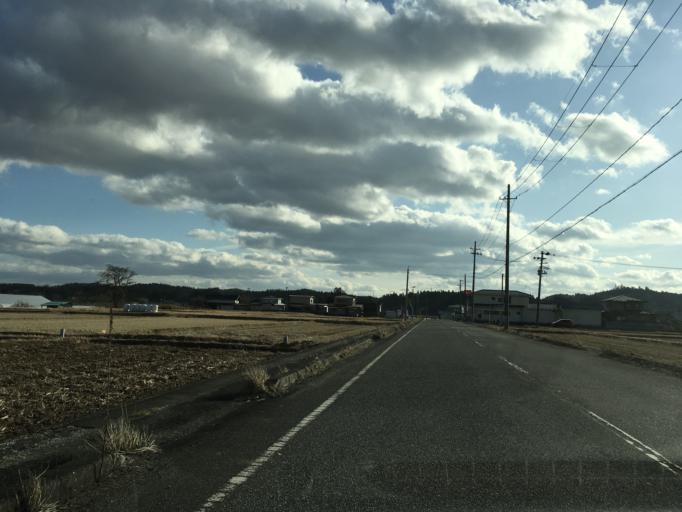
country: JP
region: Iwate
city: Ichinoseki
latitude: 38.8289
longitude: 140.9990
